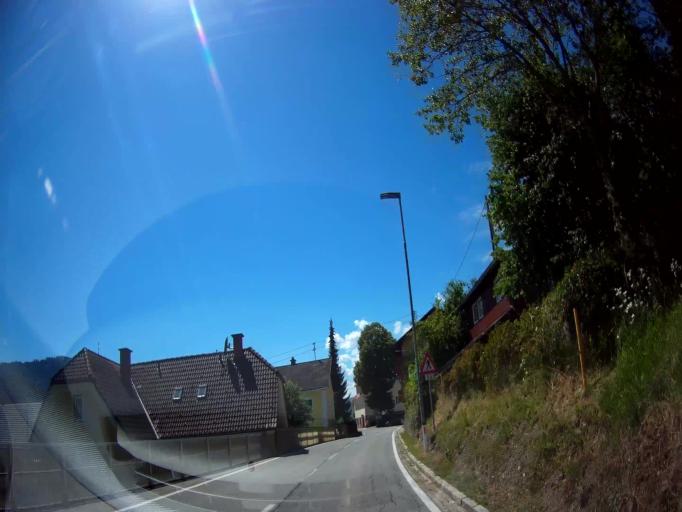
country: AT
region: Carinthia
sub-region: Politischer Bezirk Sankt Veit an der Glan
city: Glodnitz
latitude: 46.8499
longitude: 14.1941
